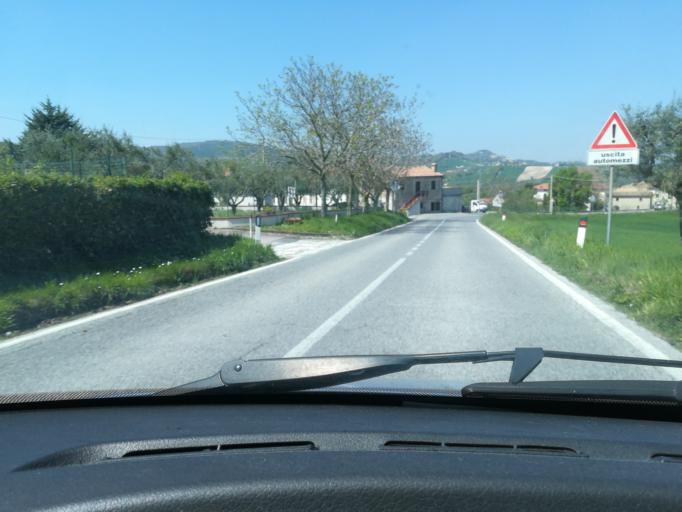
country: IT
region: The Marches
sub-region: Provincia di Macerata
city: Strada
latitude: 43.3940
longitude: 13.2069
